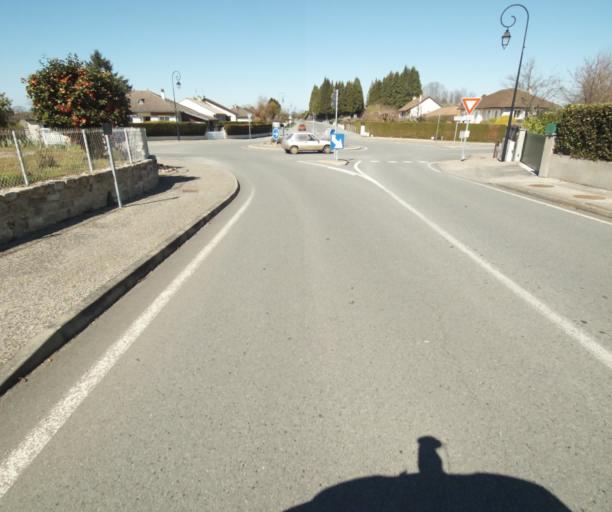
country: FR
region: Limousin
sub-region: Departement de la Correze
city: Saint-Mexant
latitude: 45.2807
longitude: 1.6600
